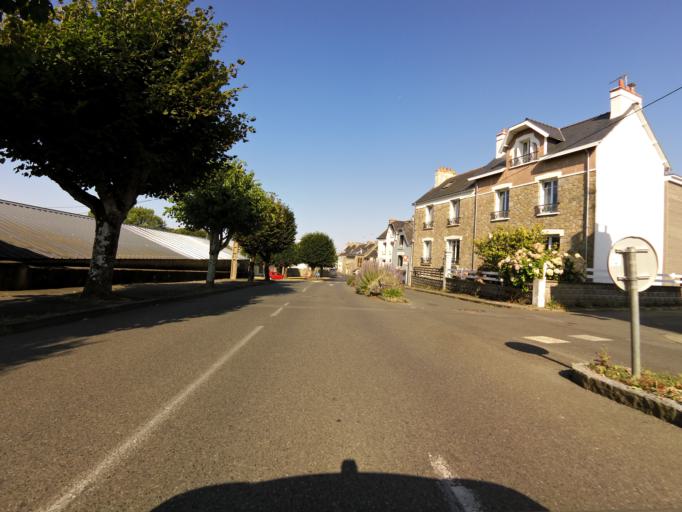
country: FR
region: Brittany
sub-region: Departement du Morbihan
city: Port-Louis
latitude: 47.7074
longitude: -3.3519
